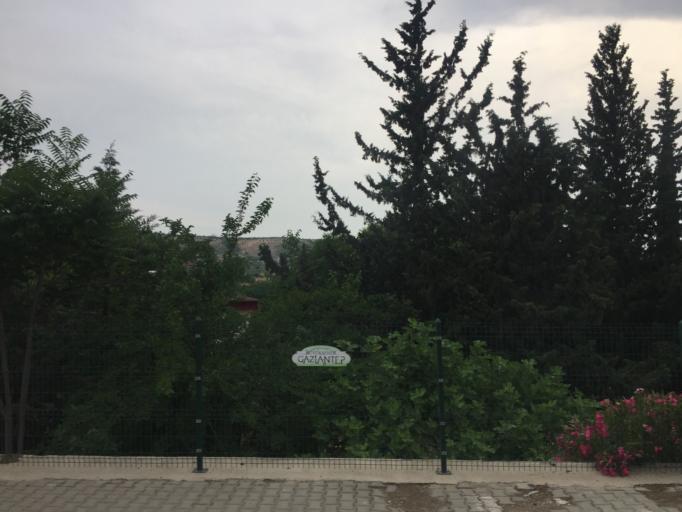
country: TR
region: Gaziantep
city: Gaziantep
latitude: 37.0062
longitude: 37.4322
